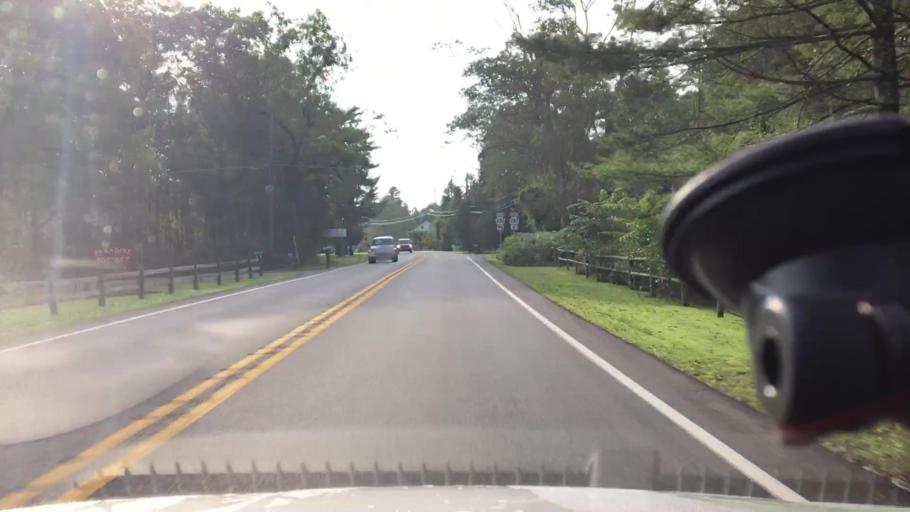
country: US
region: Pennsylvania
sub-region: Monroe County
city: Parkside
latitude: 41.1239
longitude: -75.2852
